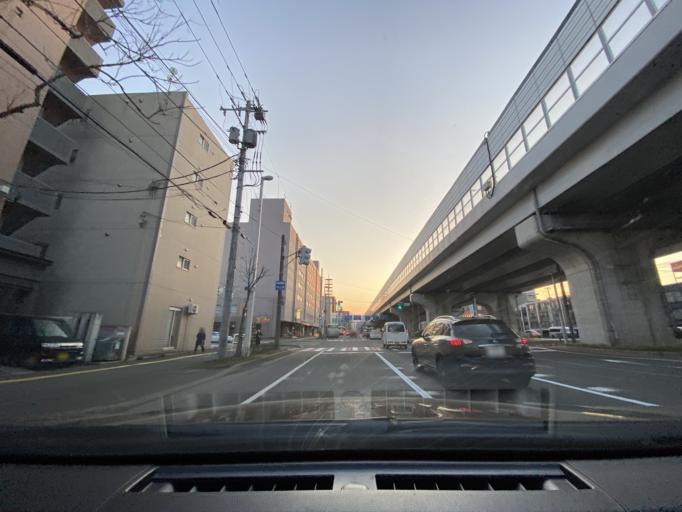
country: JP
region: Hokkaido
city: Sapporo
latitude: 43.1007
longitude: 141.3424
